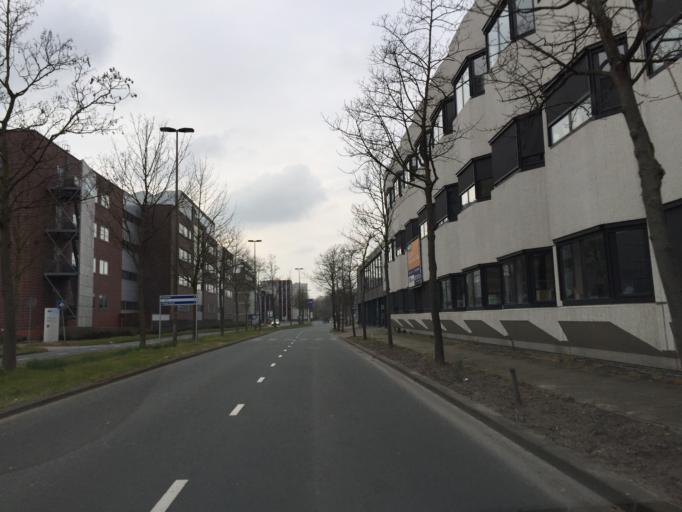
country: NL
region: South Holland
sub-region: Gemeente Delft
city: Delft
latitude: 51.9892
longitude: 4.3636
